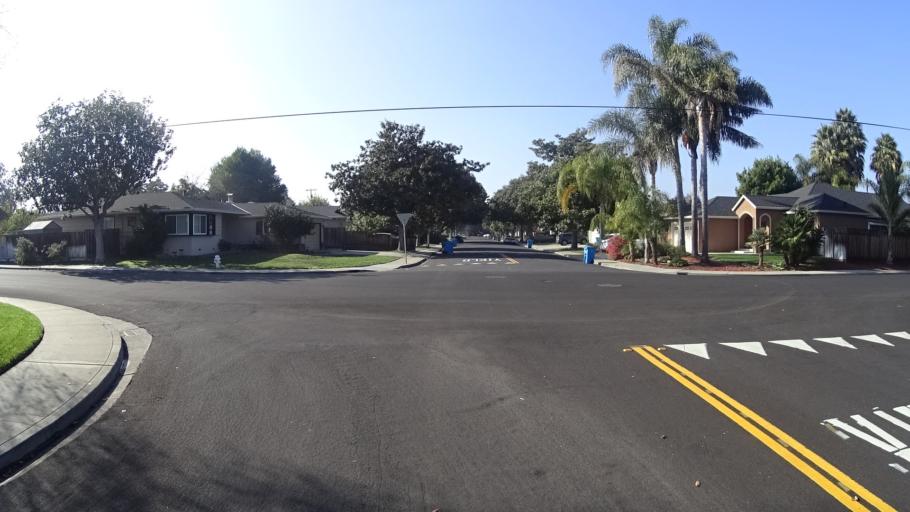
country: US
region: California
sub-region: Santa Clara County
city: Santa Clara
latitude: 37.3640
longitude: -121.9887
